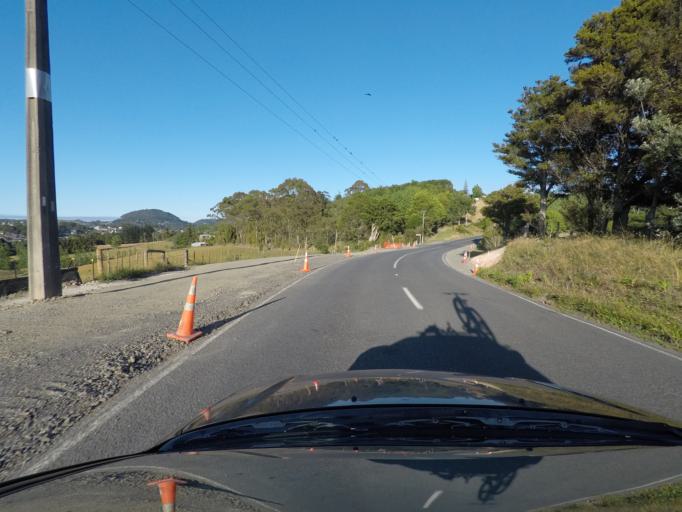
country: NZ
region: Northland
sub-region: Whangarei
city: Whangarei
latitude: -35.6665
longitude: 174.3241
